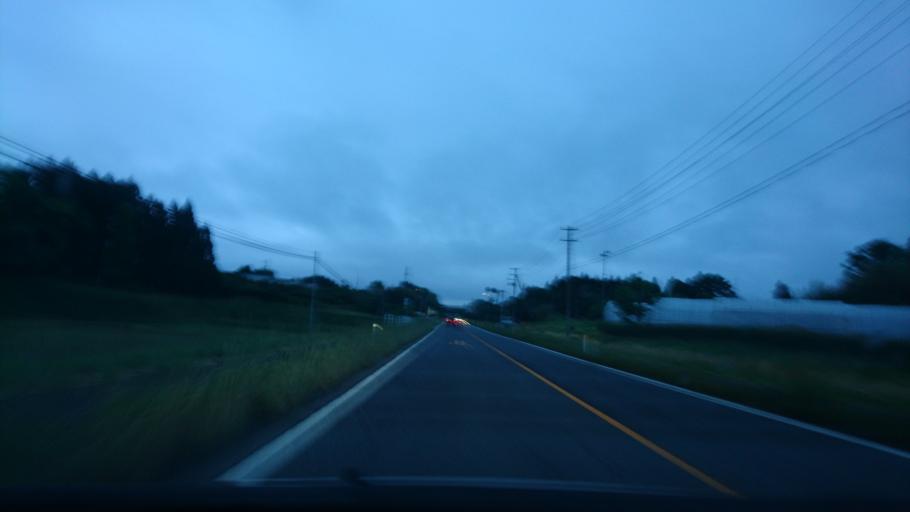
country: JP
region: Iwate
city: Ichinoseki
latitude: 38.8472
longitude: 141.0951
